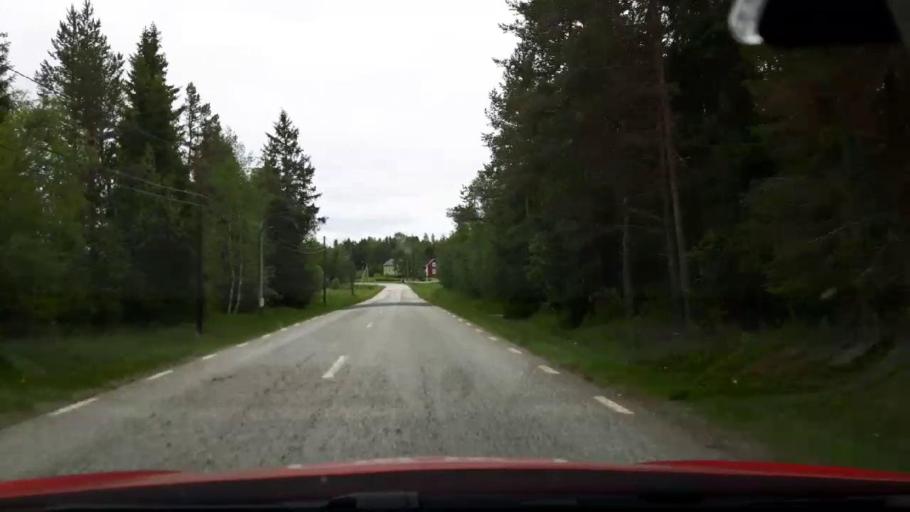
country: SE
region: Jaemtland
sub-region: Stroemsunds Kommun
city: Stroemsund
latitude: 63.3251
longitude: 15.7621
